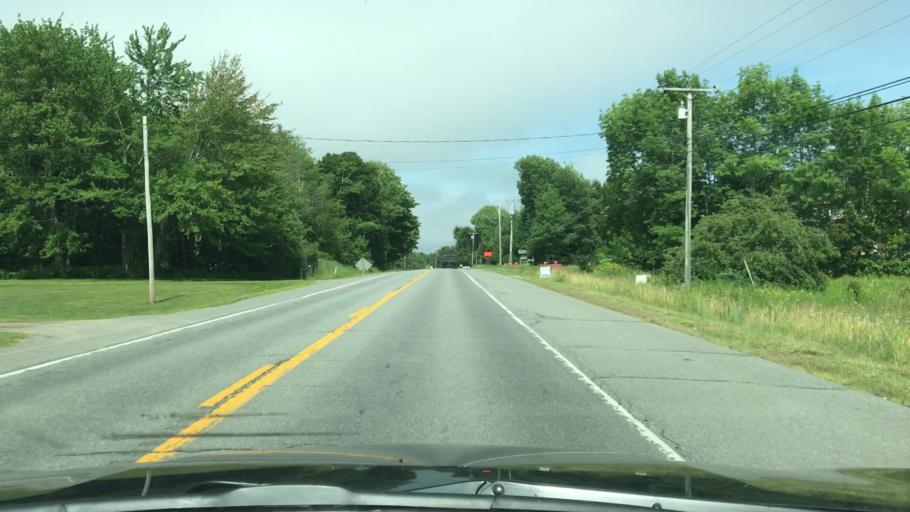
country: US
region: Maine
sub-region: Waldo County
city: Stockton Springs
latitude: 44.4809
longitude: -68.8722
